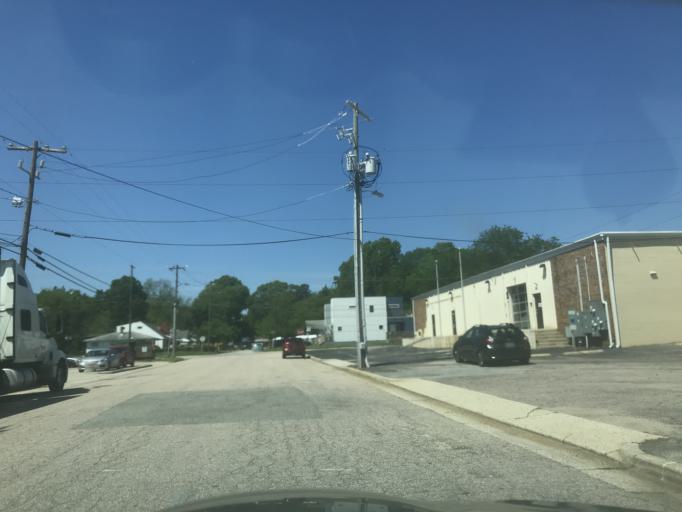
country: US
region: North Carolina
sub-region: Wake County
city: Raleigh
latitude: 35.7627
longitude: -78.6341
